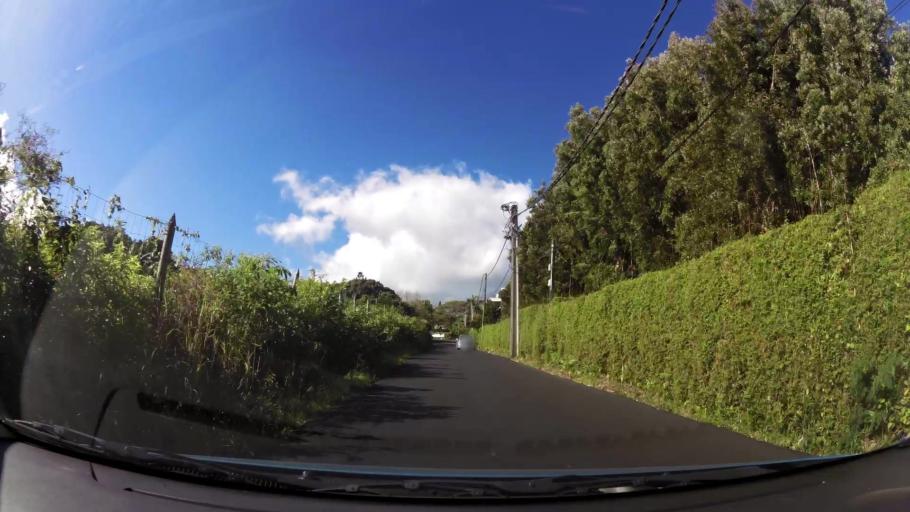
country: MU
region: Plaines Wilhems
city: Curepipe
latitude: -20.3117
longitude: 57.5039
